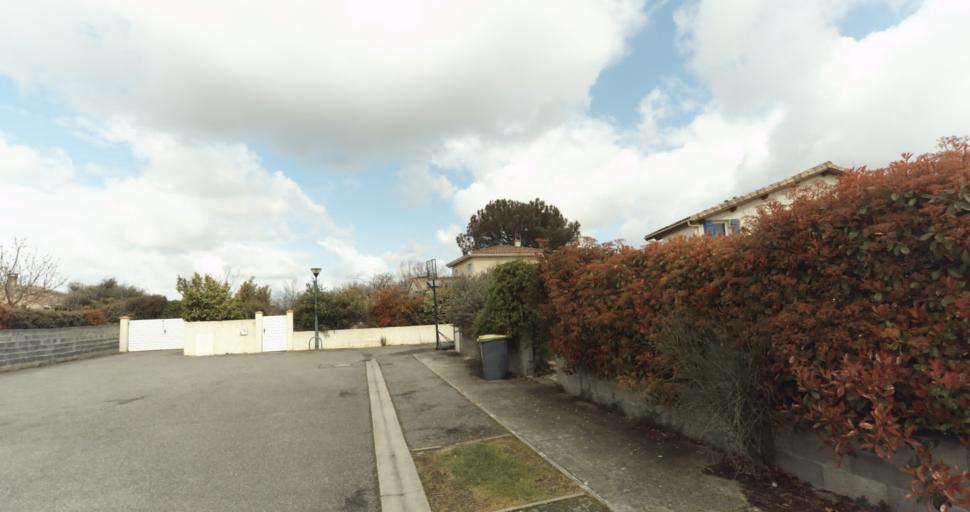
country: FR
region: Midi-Pyrenees
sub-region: Departement de la Haute-Garonne
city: Auterive
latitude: 43.3478
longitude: 1.4663
